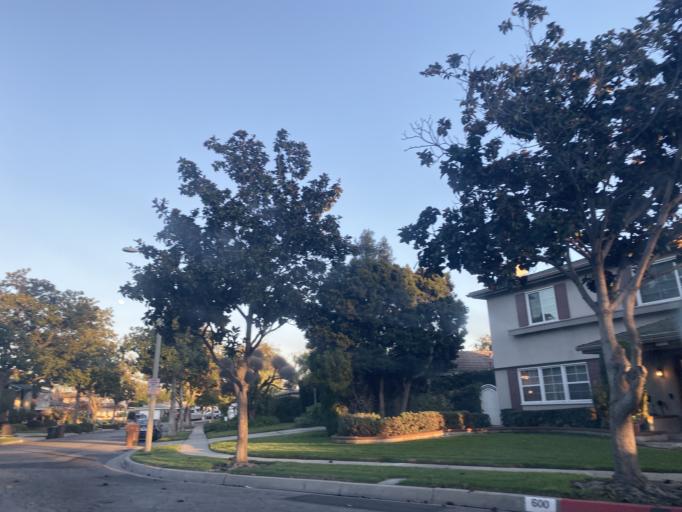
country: US
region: California
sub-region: Orange County
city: Fullerton
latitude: 33.8792
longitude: -117.9145
